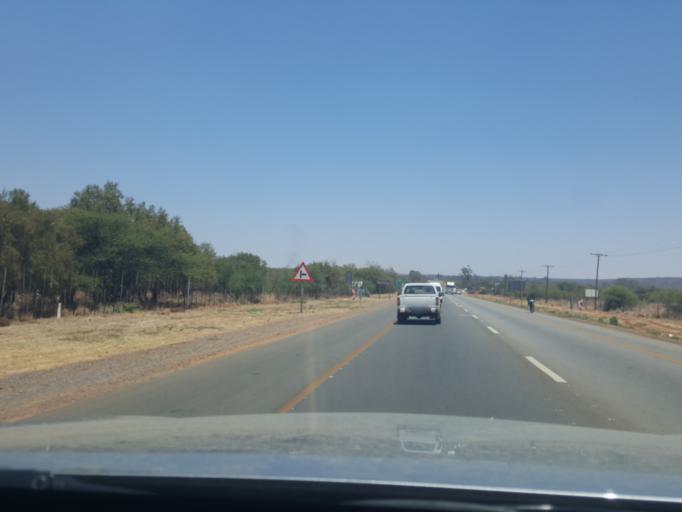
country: ZA
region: North-West
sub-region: Ngaka Modiri Molema District Municipality
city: Zeerust
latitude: -25.5577
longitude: 26.0658
